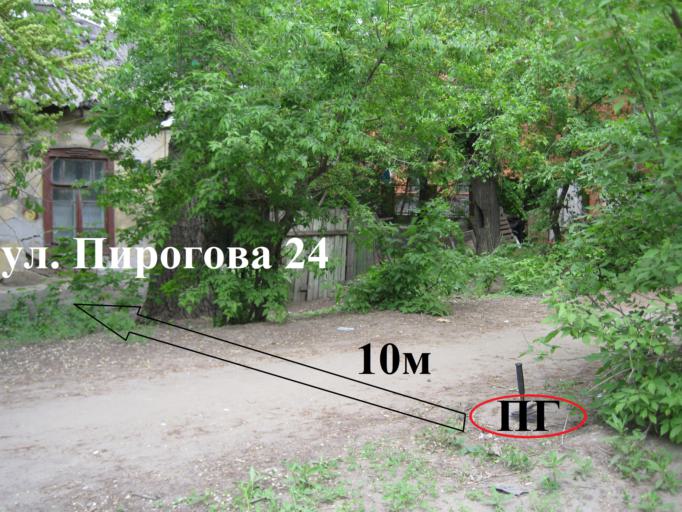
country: RU
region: Voronezj
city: Voronezh
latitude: 51.6634
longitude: 39.1713
